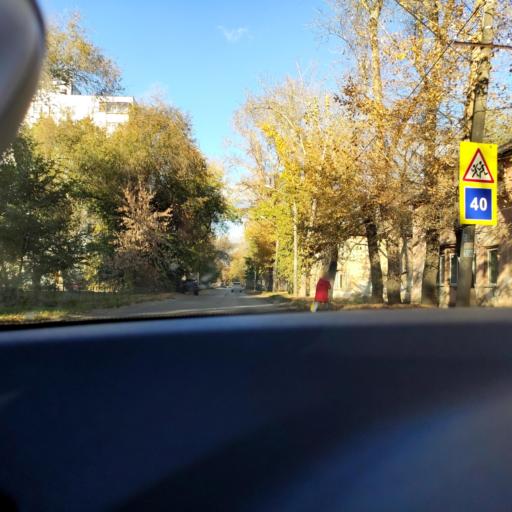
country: RU
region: Samara
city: Petra-Dubrava
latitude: 53.2324
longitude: 50.2826
